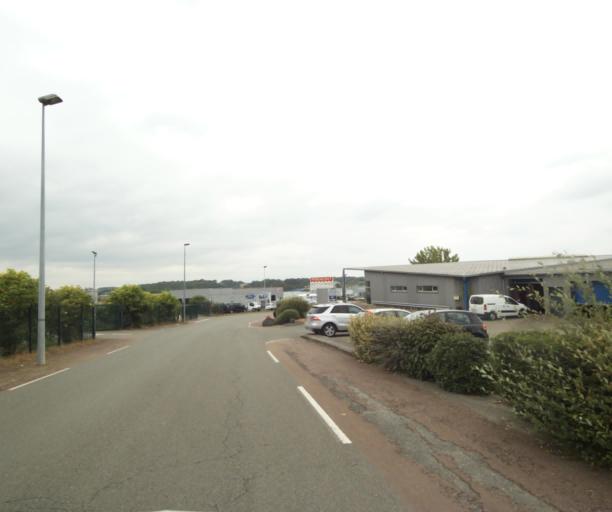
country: FR
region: Pays de la Loire
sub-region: Departement de la Sarthe
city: Solesmes
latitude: 47.8331
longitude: -0.3016
